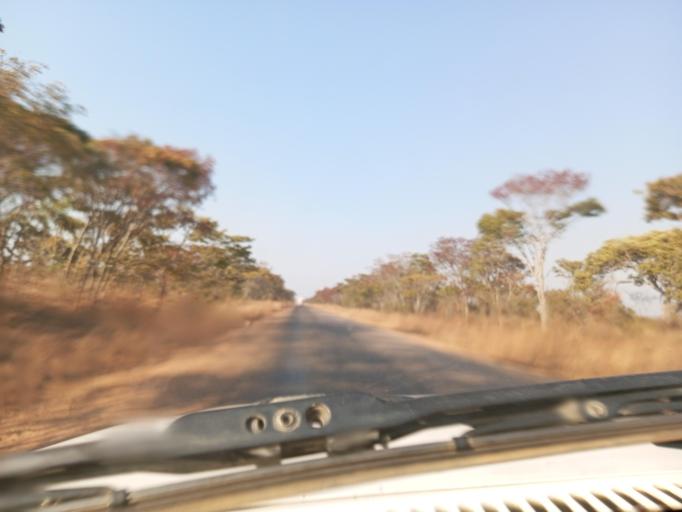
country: ZM
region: Northern
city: Mpika
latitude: -12.4079
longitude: 31.0855
